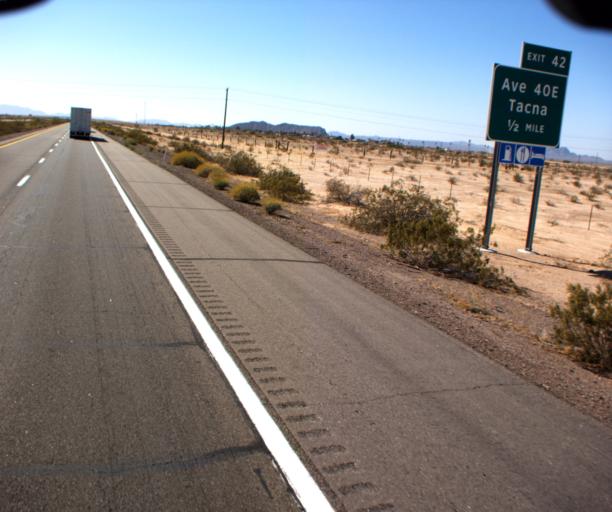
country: US
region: Arizona
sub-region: Yuma County
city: Wellton
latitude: 32.6965
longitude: -113.9346
